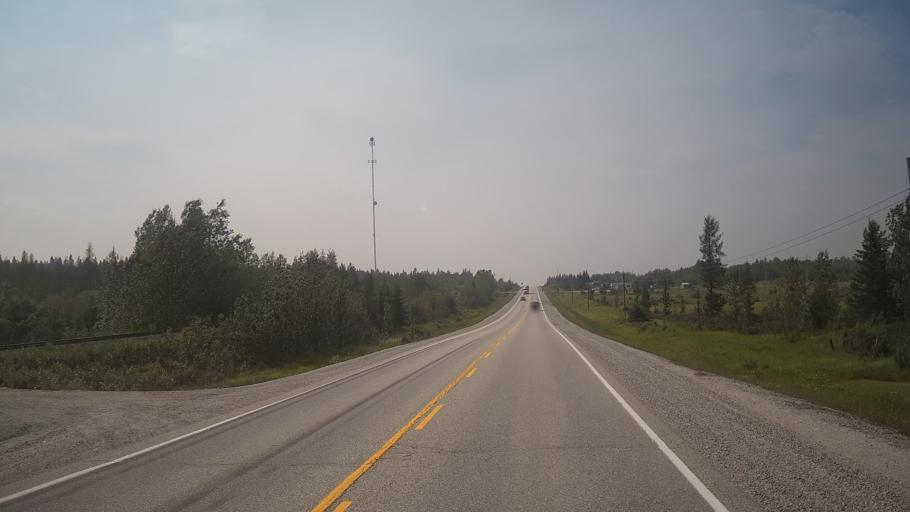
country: CA
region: Ontario
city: Kapuskasing
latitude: 49.3201
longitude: -82.0592
